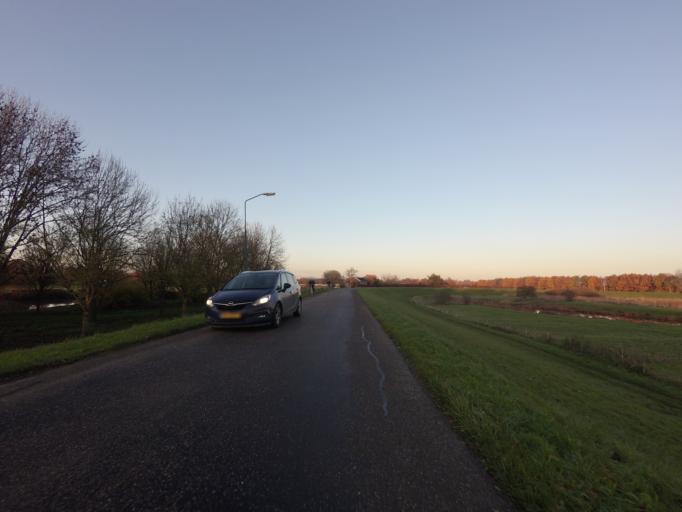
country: NL
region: Gelderland
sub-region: Gemeente Zaltbommel
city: Nederhemert-Noord
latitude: 51.7465
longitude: 5.2078
